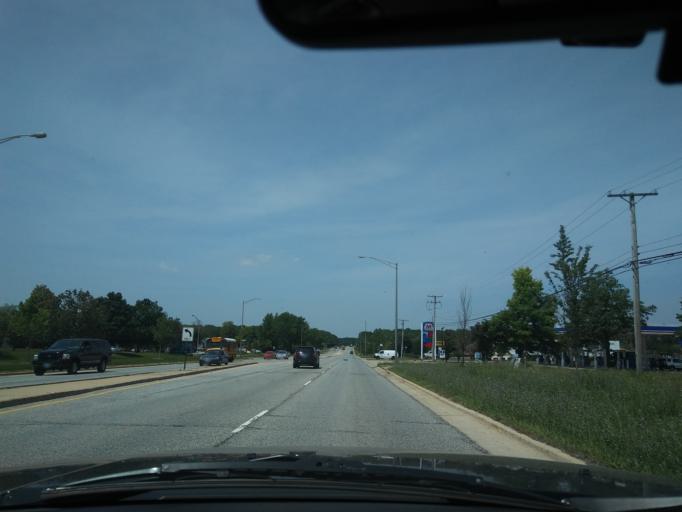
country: US
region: Illinois
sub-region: Cook County
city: Tinley Park
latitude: 41.6122
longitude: -87.7944
